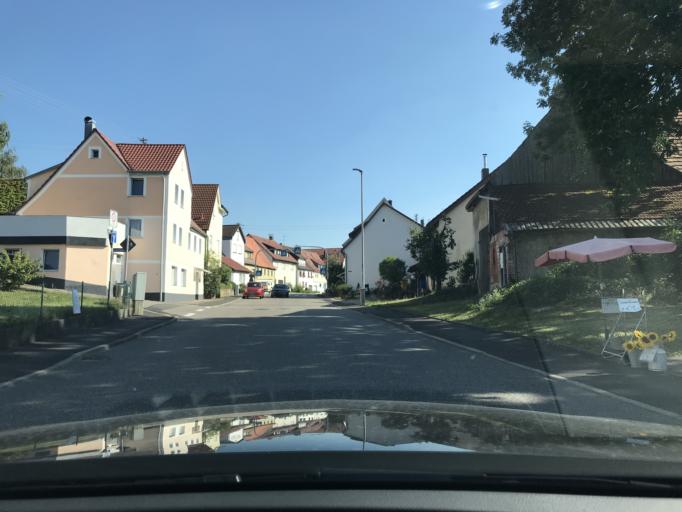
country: DE
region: Baden-Wuerttemberg
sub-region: Regierungsbezirk Stuttgart
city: Winterbach
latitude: 48.7736
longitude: 9.5028
